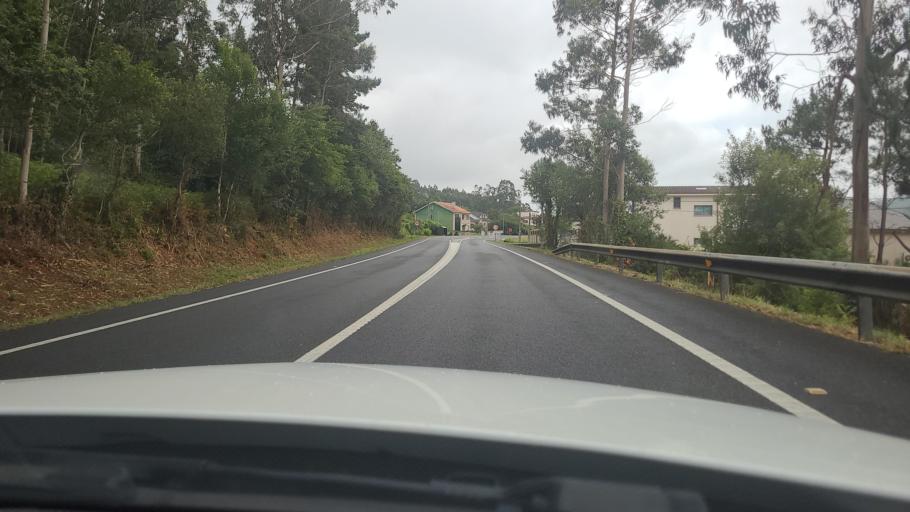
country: ES
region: Galicia
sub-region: Provincia da Coruna
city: Cee
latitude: 42.9979
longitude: -9.1788
